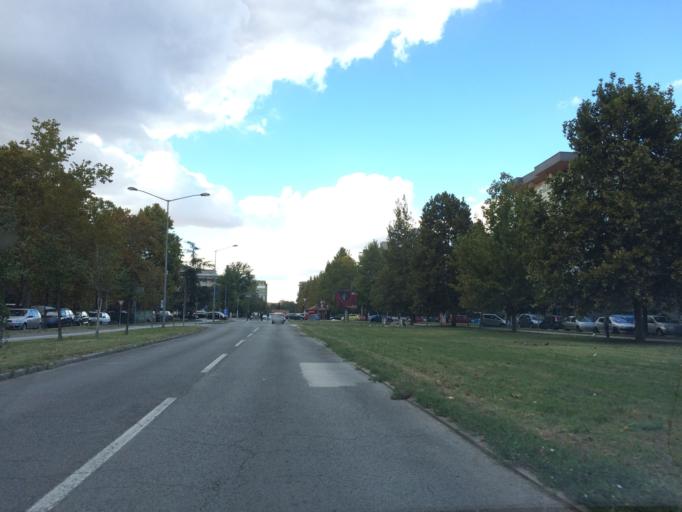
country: RS
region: Autonomna Pokrajina Vojvodina
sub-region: Juznobacki Okrug
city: Novi Sad
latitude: 45.2377
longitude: 19.8331
